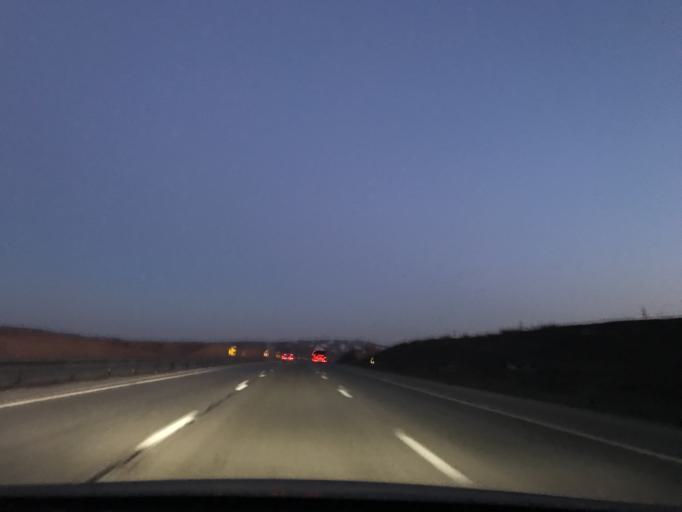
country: IR
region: Isfahan
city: Kashan
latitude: 33.8260
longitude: 51.6240
